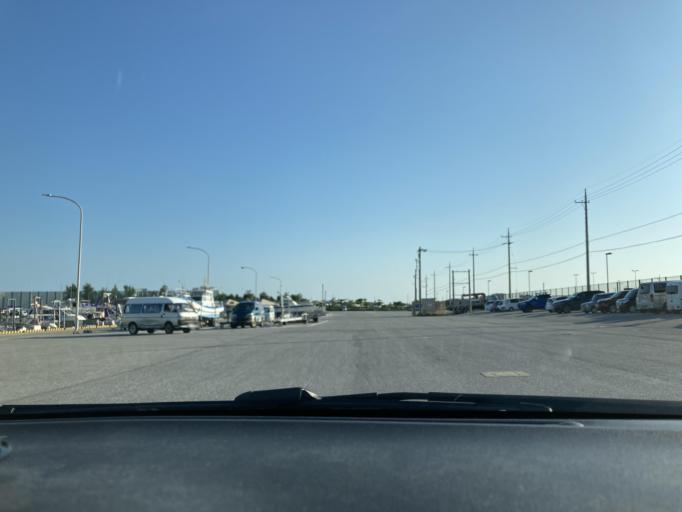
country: JP
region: Okinawa
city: Naha-shi
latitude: 26.2185
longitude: 127.6628
